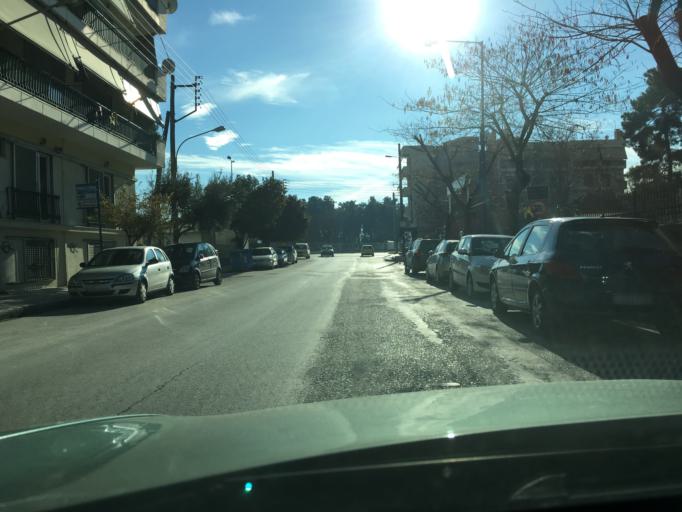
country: GR
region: Thessaly
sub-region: Nomos Larisis
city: Larisa
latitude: 39.6338
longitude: 22.4074
